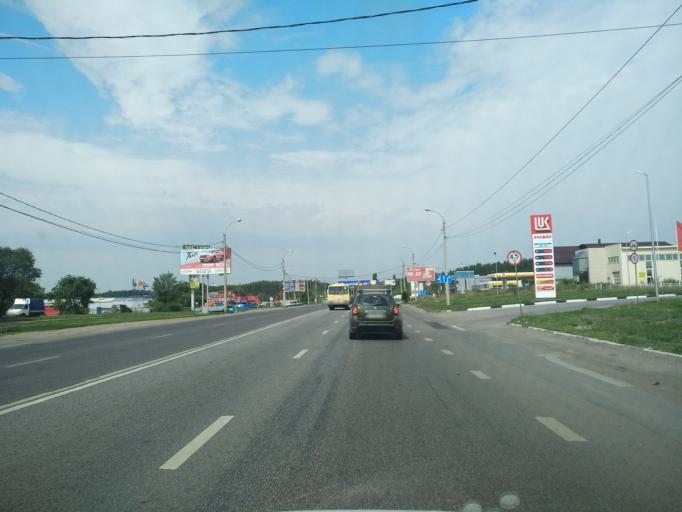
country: RU
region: Voronezj
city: Somovo
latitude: 51.6801
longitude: 39.2870
